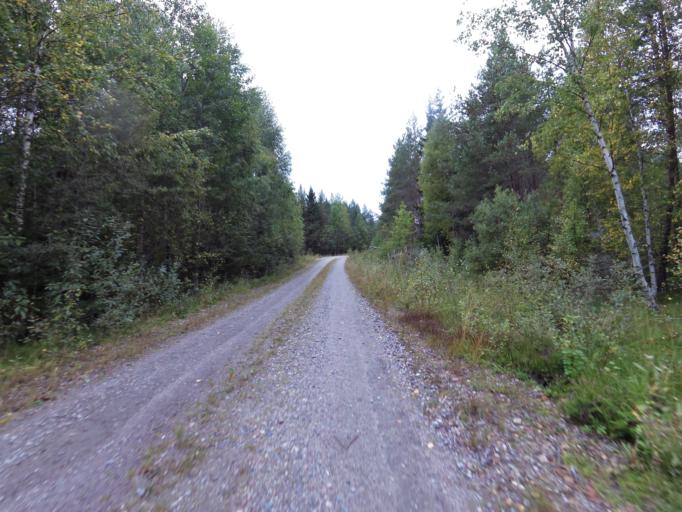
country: SE
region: Gaevleborg
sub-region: Gavle Kommun
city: Valbo
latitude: 60.7447
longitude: 17.0141
